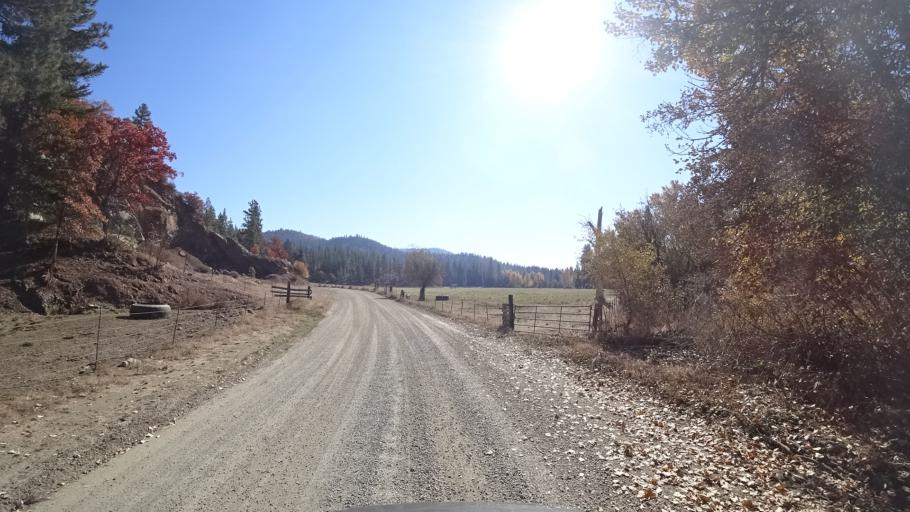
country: US
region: California
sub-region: Siskiyou County
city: Yreka
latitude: 41.6188
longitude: -122.9647
